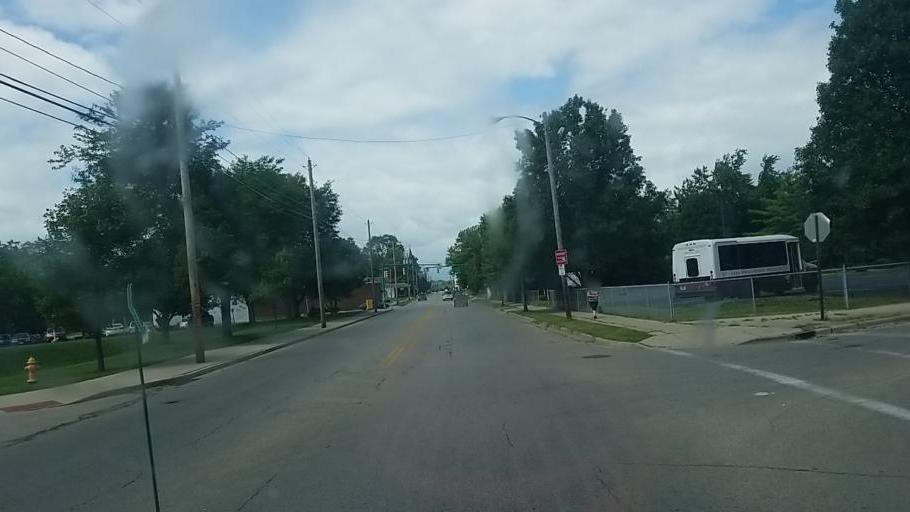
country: US
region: Ohio
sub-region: Clark County
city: Springfield
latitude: 39.9140
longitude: -83.7999
